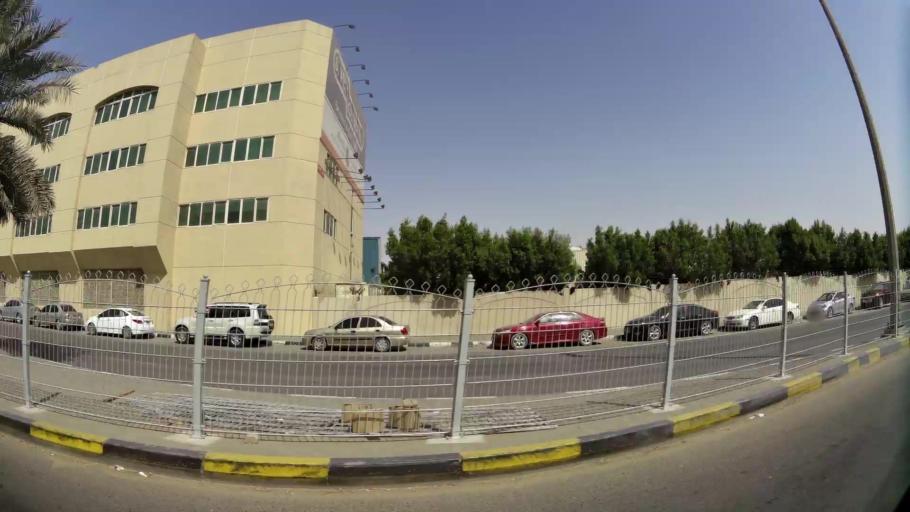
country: AE
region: Ash Shariqah
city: Sharjah
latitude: 25.3111
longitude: 55.4224
